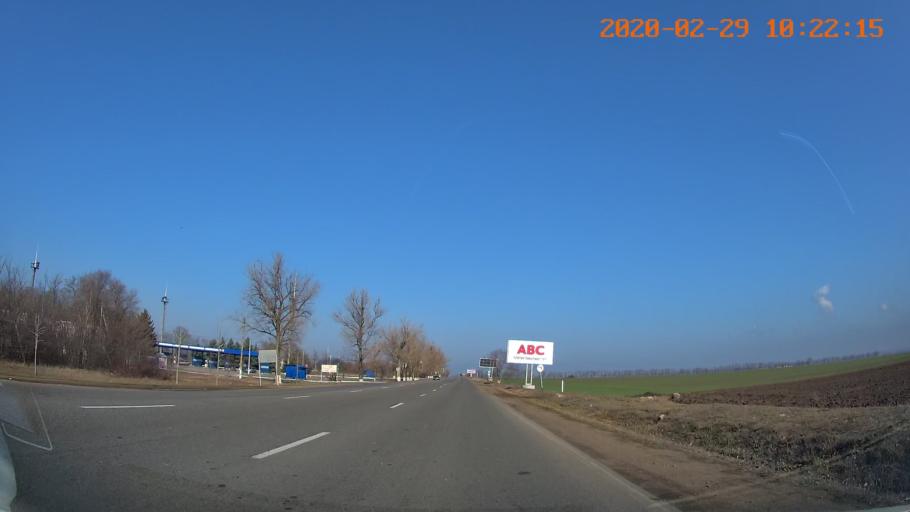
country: MD
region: Telenesti
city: Tiraspolul Nou
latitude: 46.8739
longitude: 29.6075
